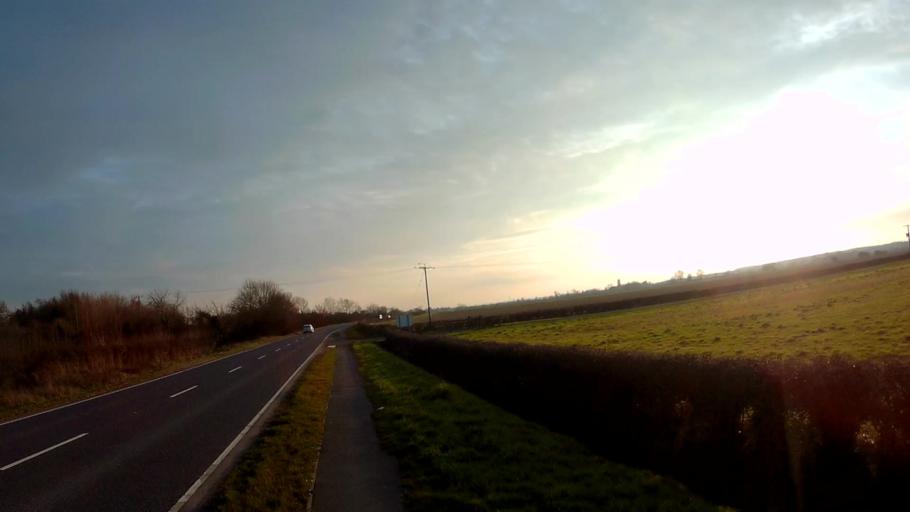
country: GB
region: England
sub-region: Lincolnshire
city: Bourne
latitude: 52.7939
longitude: -0.3764
